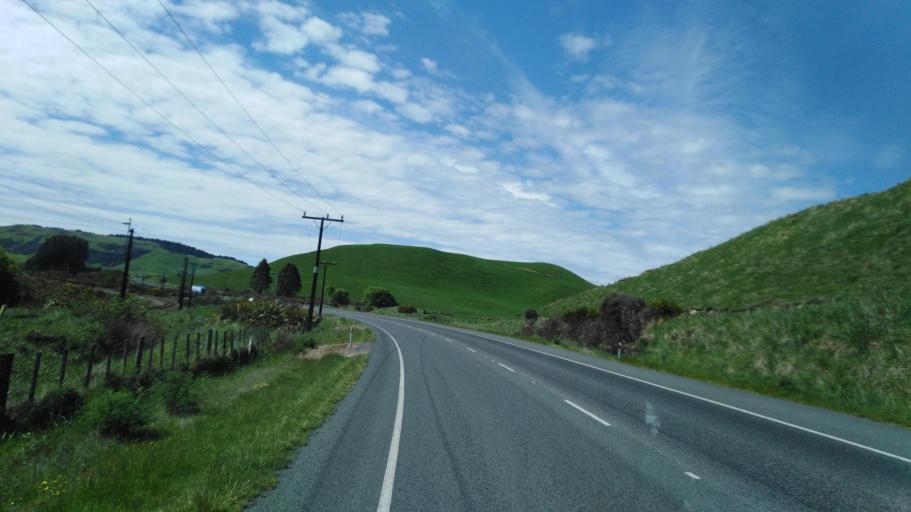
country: NZ
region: Manawatu-Wanganui
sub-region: Ruapehu District
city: Waiouru
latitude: -39.5058
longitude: 175.6757
